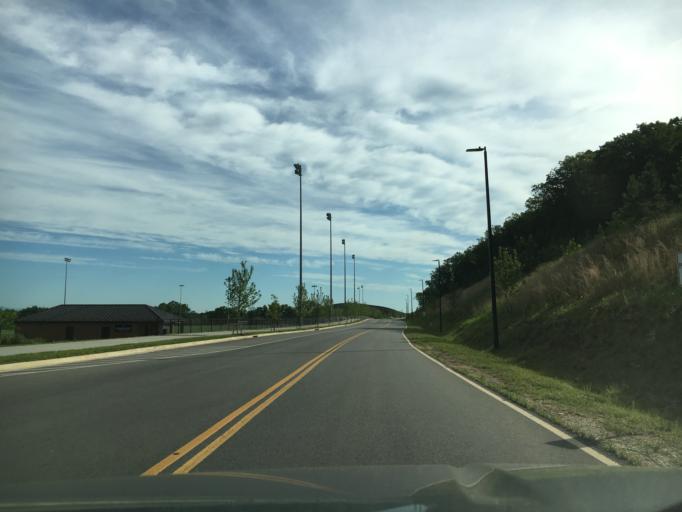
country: US
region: Virginia
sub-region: City of Lynchburg
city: West Lynchburg
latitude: 37.3563
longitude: -79.1665
